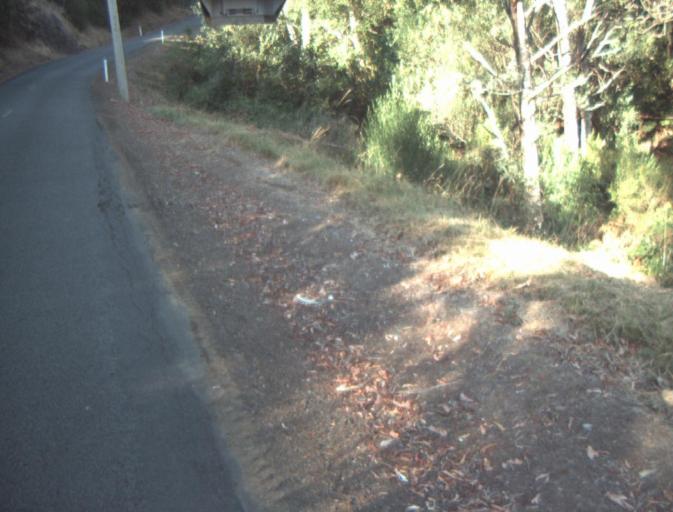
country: AU
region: Tasmania
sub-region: Launceston
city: Mayfield
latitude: -41.2959
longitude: 147.2016
